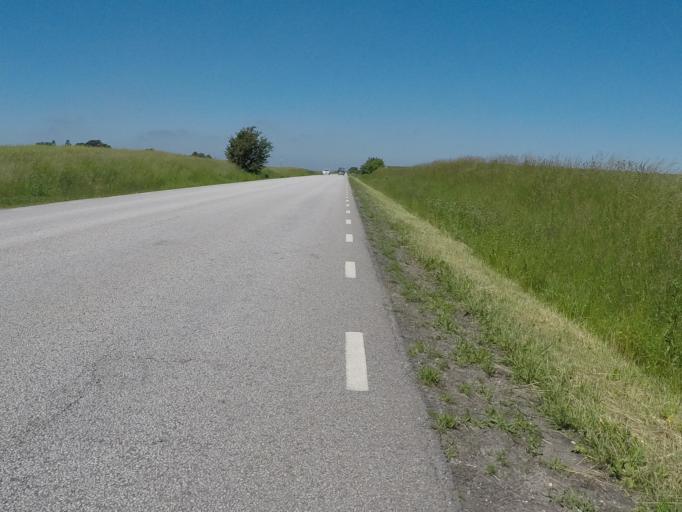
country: SE
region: Skane
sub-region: Malmo
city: Oxie
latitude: 55.5592
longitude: 13.1013
